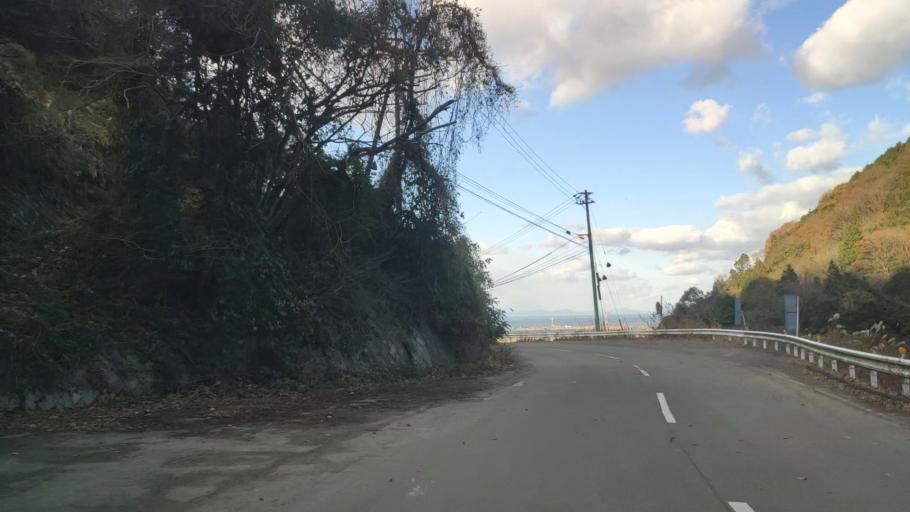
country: JP
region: Ehime
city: Saijo
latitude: 33.8791
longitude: 133.1335
